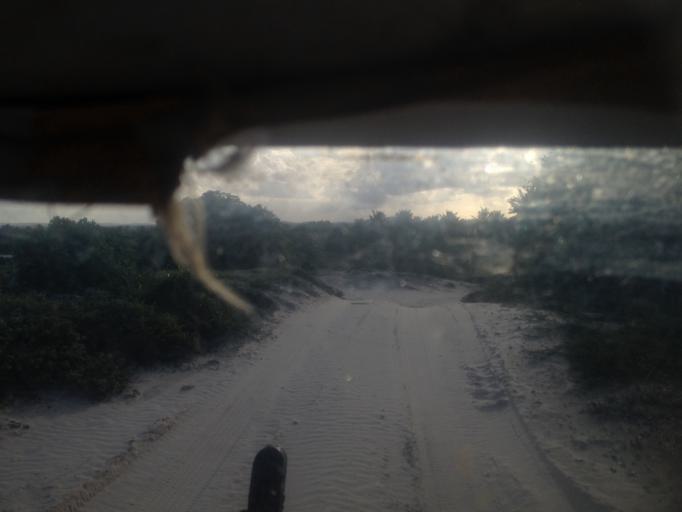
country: BR
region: Sergipe
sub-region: Indiaroba
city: Indiaroba
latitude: -11.4686
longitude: -37.3691
